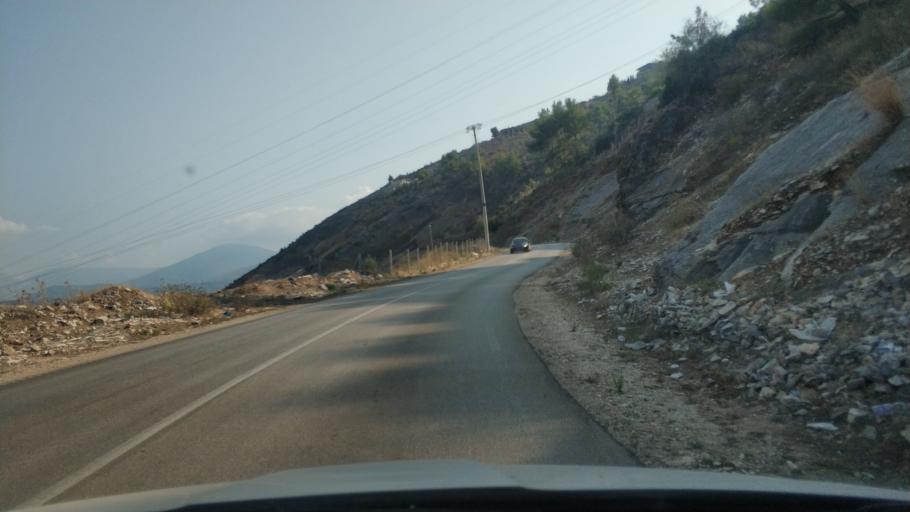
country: AL
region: Vlore
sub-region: Rrethi i Sarandes
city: Sarande
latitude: 39.8690
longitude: 20.0309
